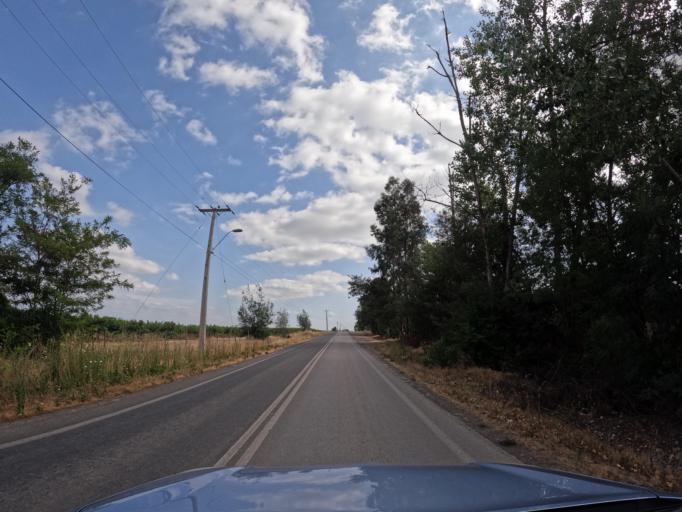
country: CL
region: Maule
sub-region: Provincia de Curico
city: Molina
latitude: -35.1714
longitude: -71.2922
